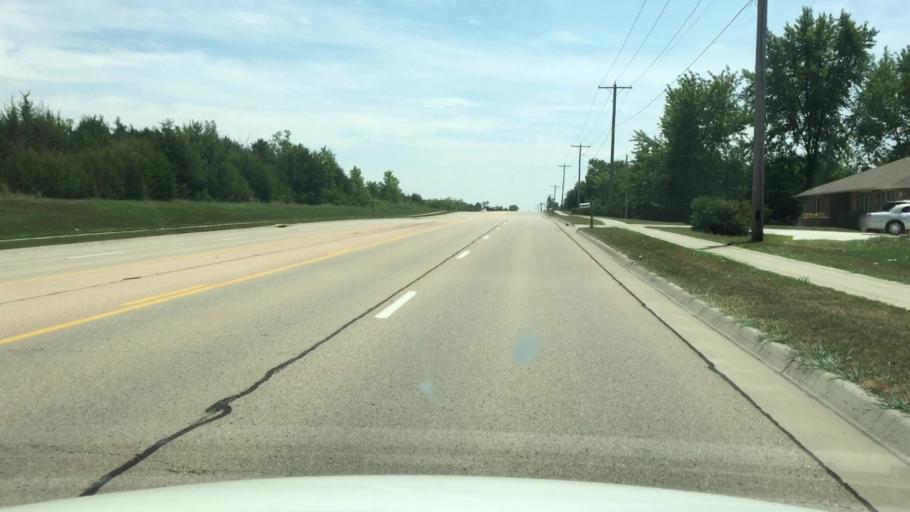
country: US
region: Kansas
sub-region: Shawnee County
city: Topeka
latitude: 38.9946
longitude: -95.6145
